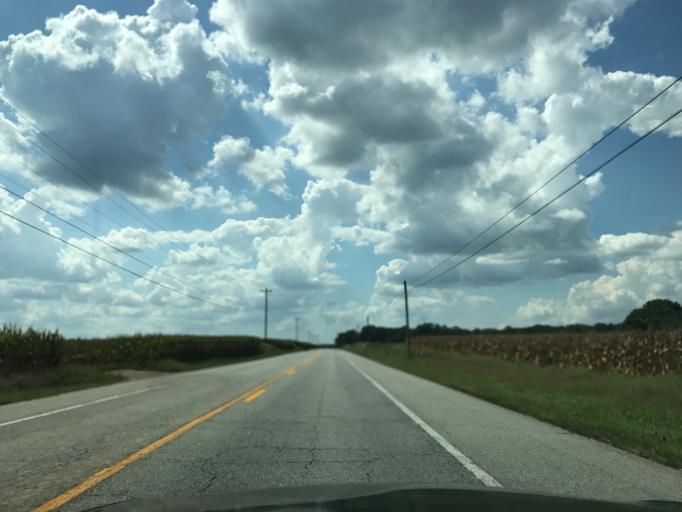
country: US
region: Maryland
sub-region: Queen Anne's County
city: Kingstown
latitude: 39.1830
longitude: -75.8988
